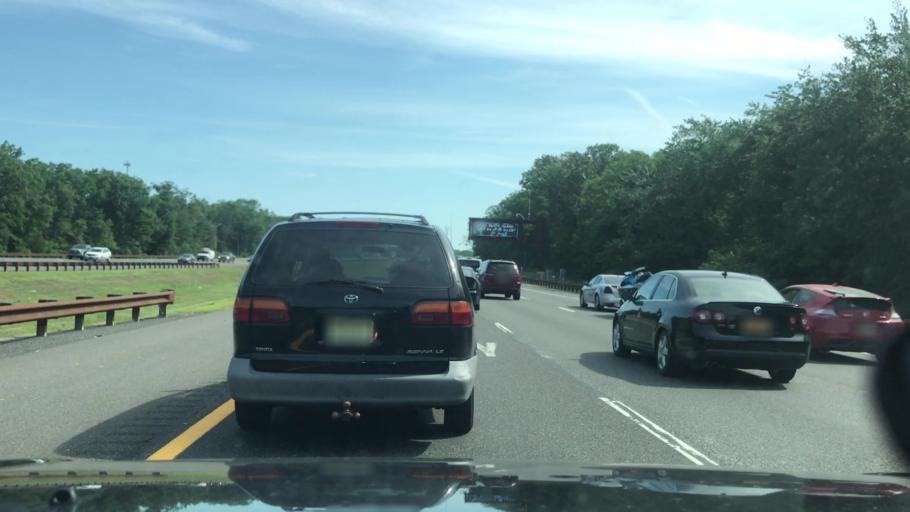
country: US
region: New Jersey
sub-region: Ocean County
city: Leisure Village
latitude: 40.0213
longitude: -74.1846
